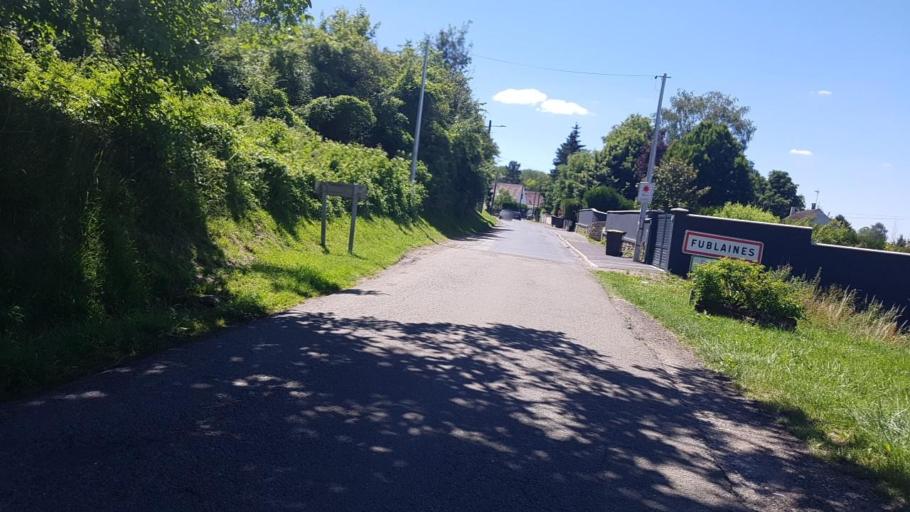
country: FR
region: Ile-de-France
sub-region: Departement de Seine-et-Marne
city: Fublaines
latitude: 48.9393
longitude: 2.9458
